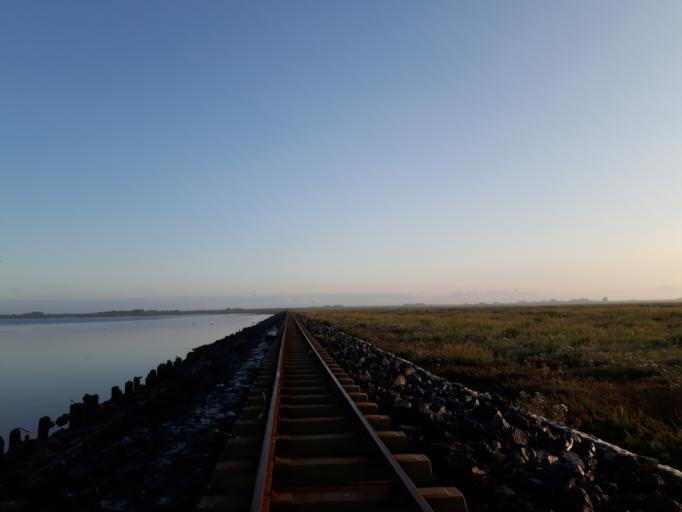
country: DE
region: Schleswig-Holstein
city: Dagebull
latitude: 54.7120
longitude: 8.7113
